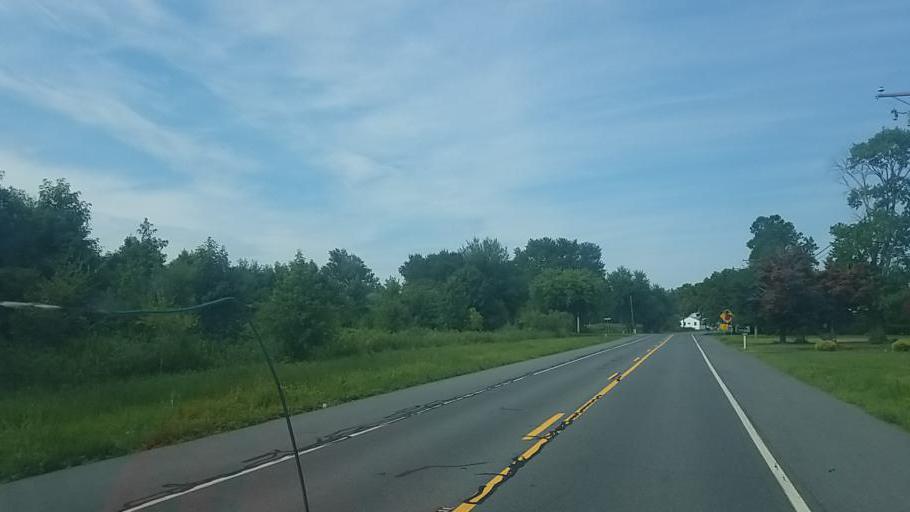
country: US
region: Delaware
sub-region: Sussex County
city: Selbyville
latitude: 38.5286
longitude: -75.1969
